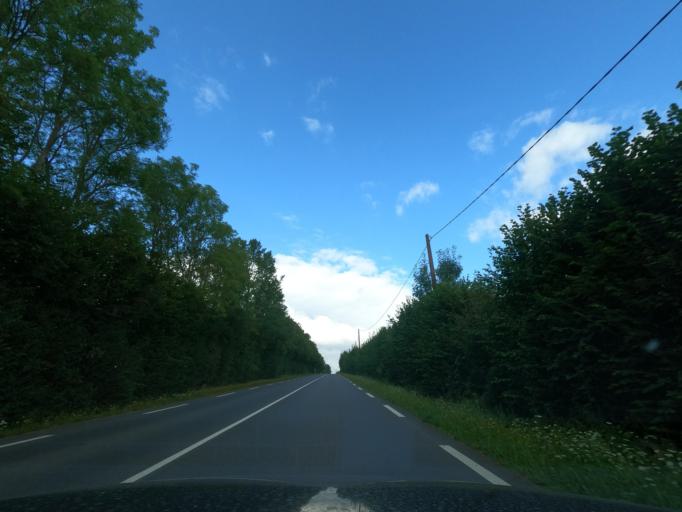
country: FR
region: Lower Normandy
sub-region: Departement de l'Orne
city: Gace
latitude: 48.8151
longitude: 0.3130
